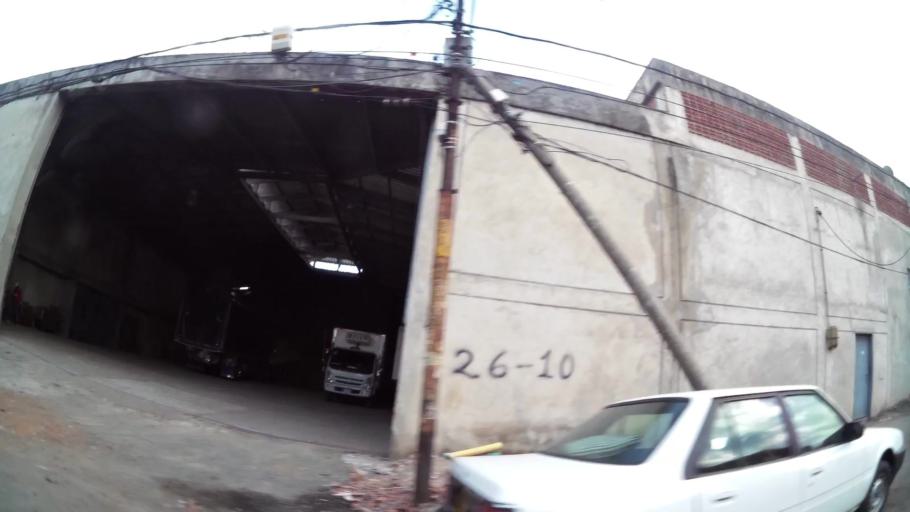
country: CO
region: Valle del Cauca
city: Cali
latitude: 3.4563
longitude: -76.5186
